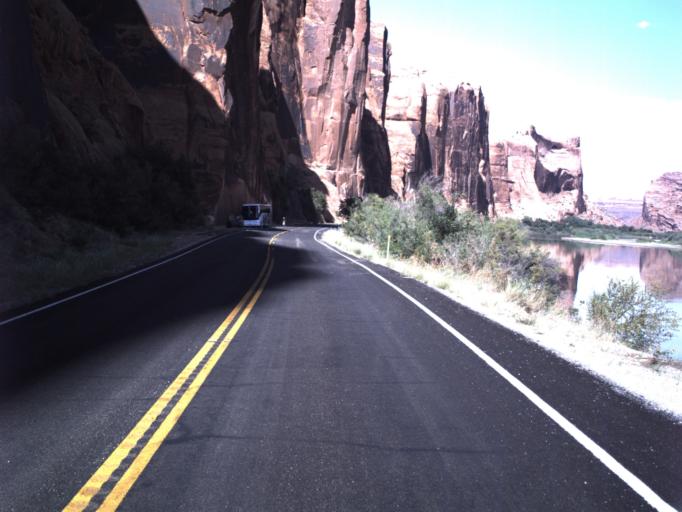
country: US
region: Utah
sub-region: Grand County
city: Moab
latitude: 38.5430
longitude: -109.6006
